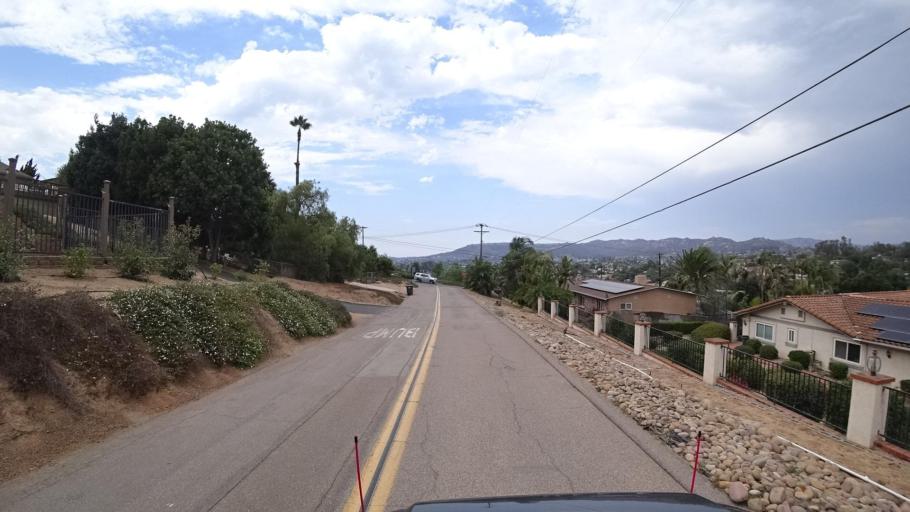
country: US
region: California
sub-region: San Diego County
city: Escondido
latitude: 33.1394
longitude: -117.1138
